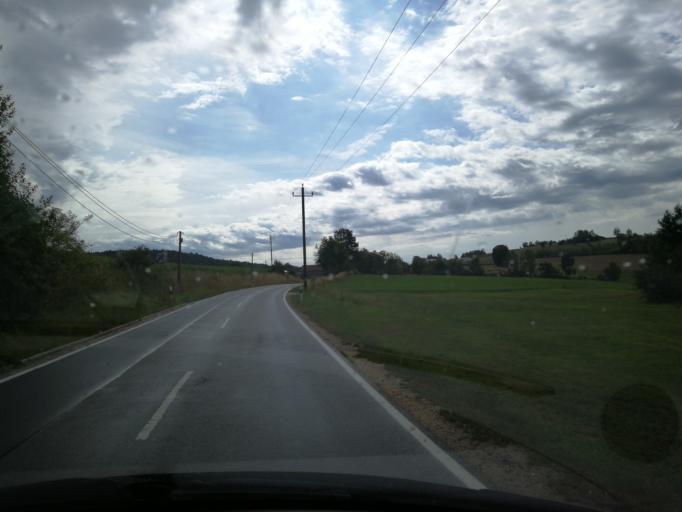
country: DE
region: Bavaria
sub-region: Upper Palatinate
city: Brennberg
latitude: 49.0658
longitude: 12.3615
